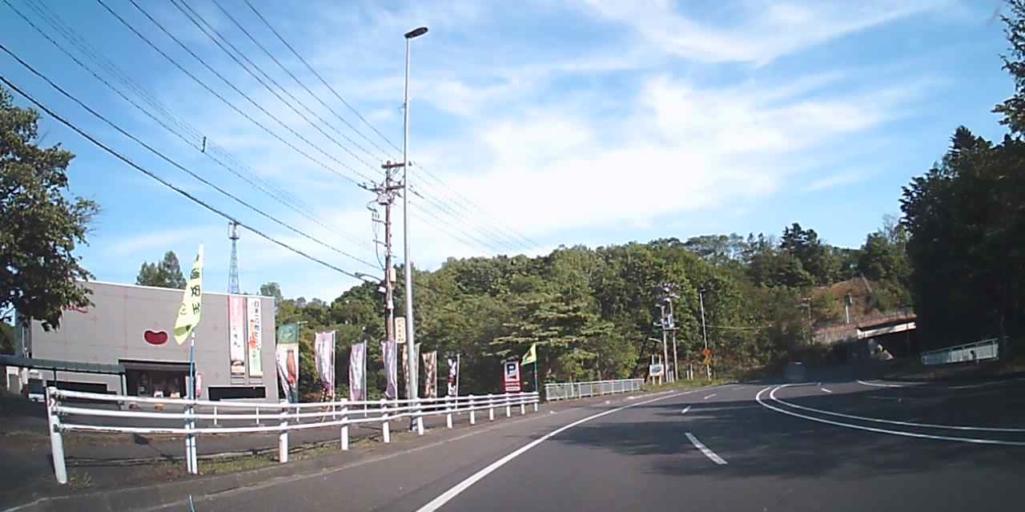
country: JP
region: Hokkaido
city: Shiraoi
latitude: 42.4649
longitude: 141.1778
